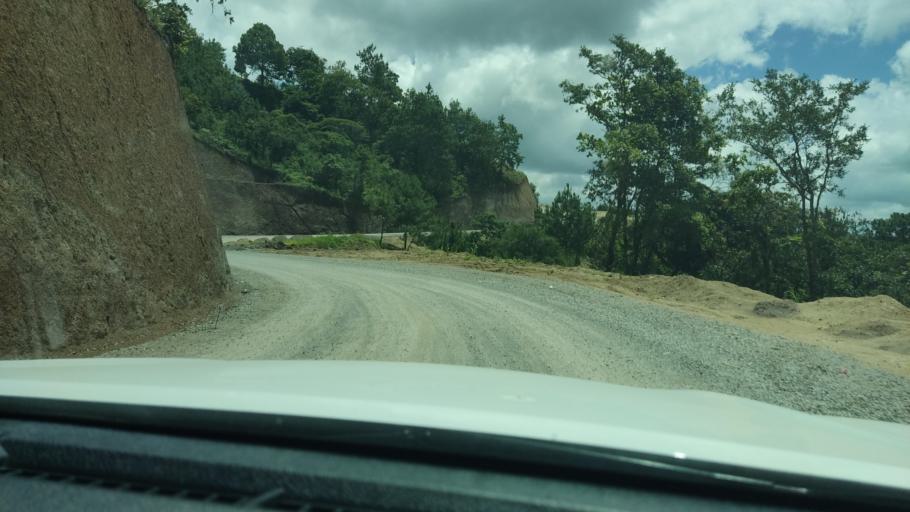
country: GT
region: Chimaltenango
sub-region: Municipio de San Juan Comalapa
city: Comalapa
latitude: 14.7884
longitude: -90.8612
